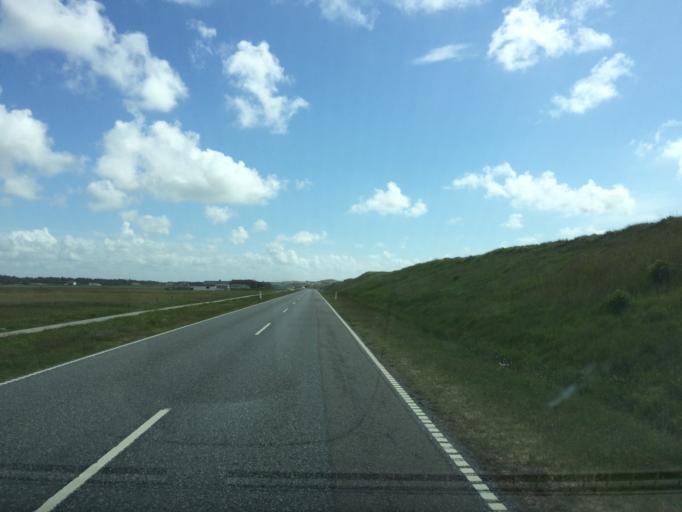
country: DK
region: Central Jutland
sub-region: Holstebro Kommune
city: Ulfborg
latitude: 56.3295
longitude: 8.1230
